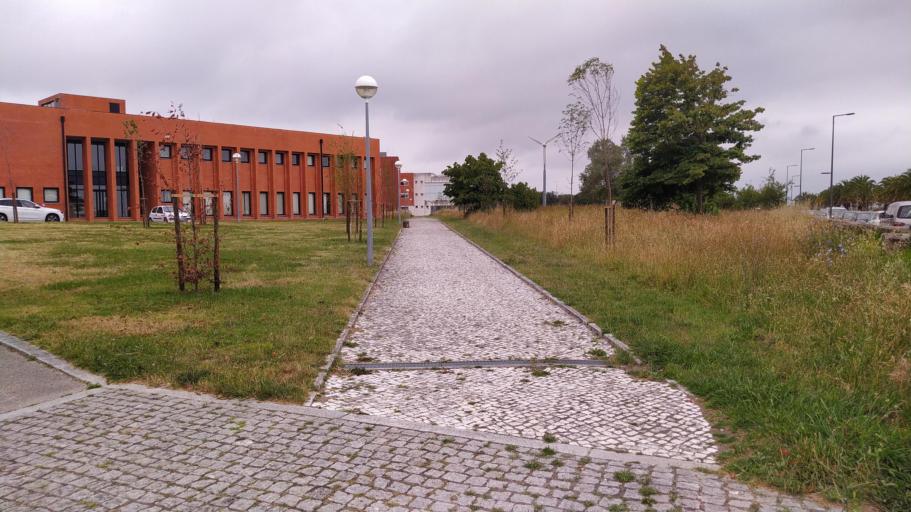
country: PT
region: Aveiro
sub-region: Aveiro
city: Aveiro
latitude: 40.6348
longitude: -8.6603
